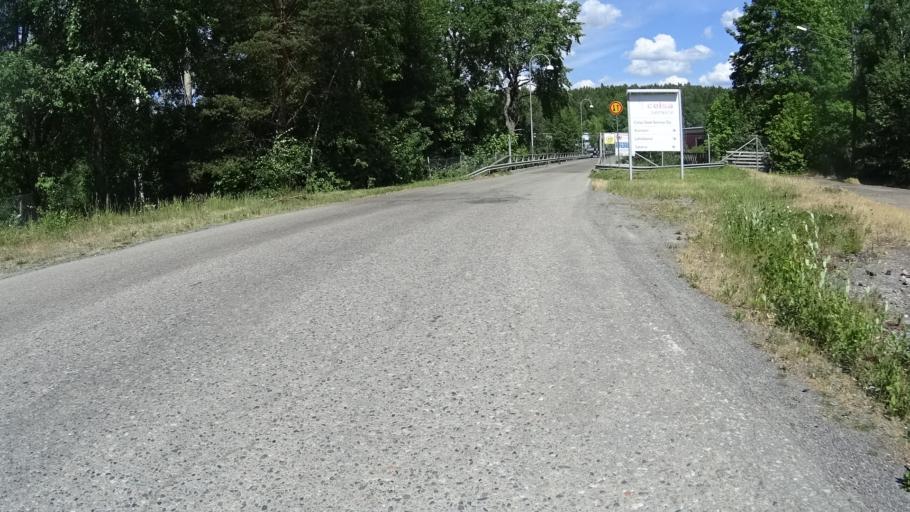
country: FI
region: Uusimaa
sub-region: Raaseporin
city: Pohja
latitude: 60.0921
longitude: 23.5654
